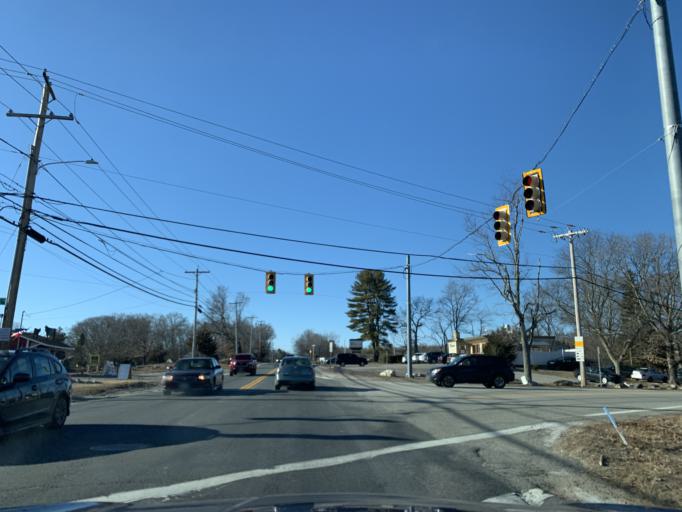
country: US
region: Rhode Island
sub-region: Providence County
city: Smithfield
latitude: 41.9018
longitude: -71.5043
